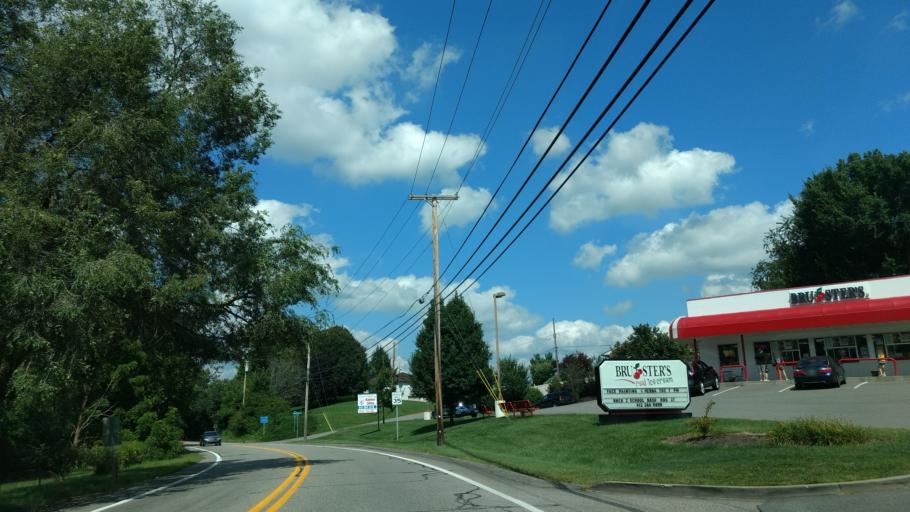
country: US
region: Pennsylvania
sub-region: Allegheny County
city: Franklin Park
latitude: 40.5823
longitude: -80.0375
